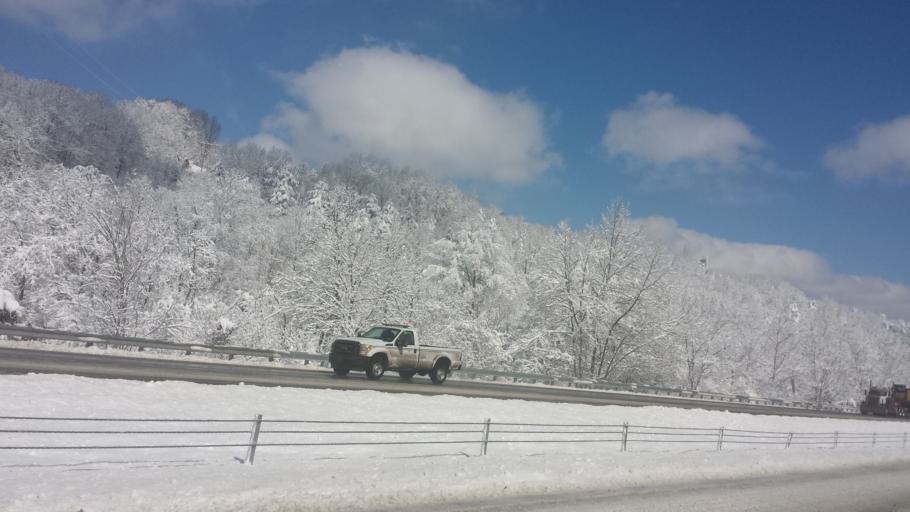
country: US
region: West Virginia
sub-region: Jackson County
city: Ripley
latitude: 38.7938
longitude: -81.7188
